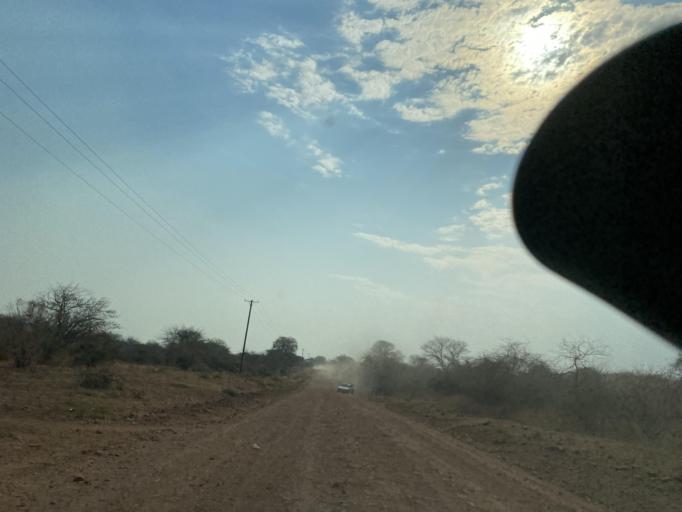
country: ZW
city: Chirundu
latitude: -15.9186
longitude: 28.9810
